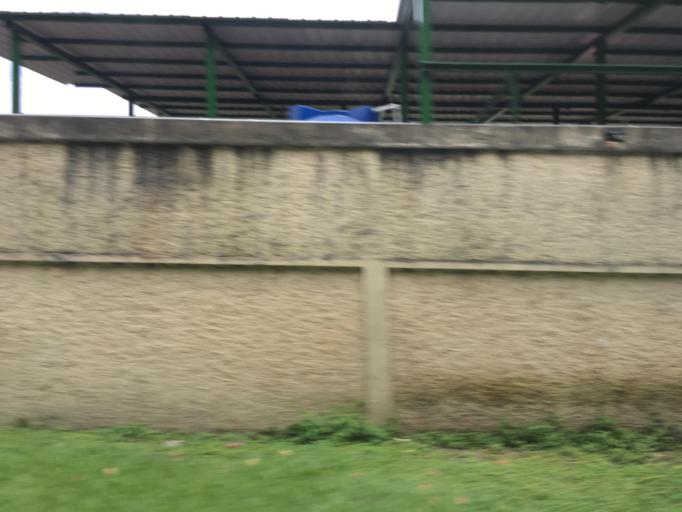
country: GT
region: Guatemala
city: Villa Canales
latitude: 14.4443
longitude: -90.5287
